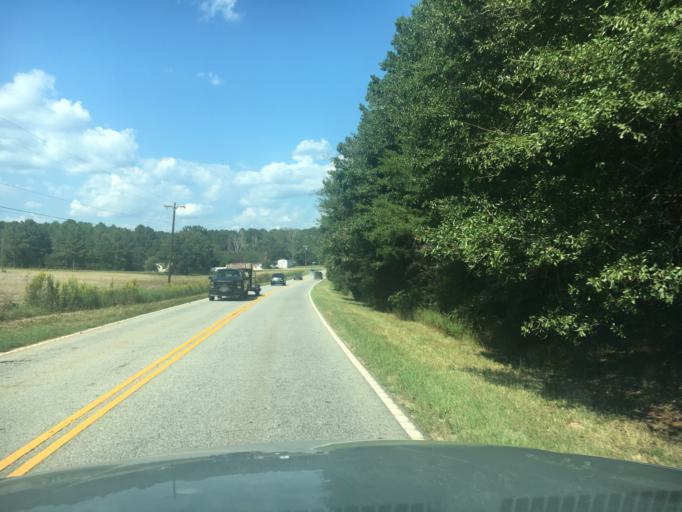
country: US
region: South Carolina
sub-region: Anderson County
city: Pendleton
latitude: 34.6085
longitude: -82.7897
